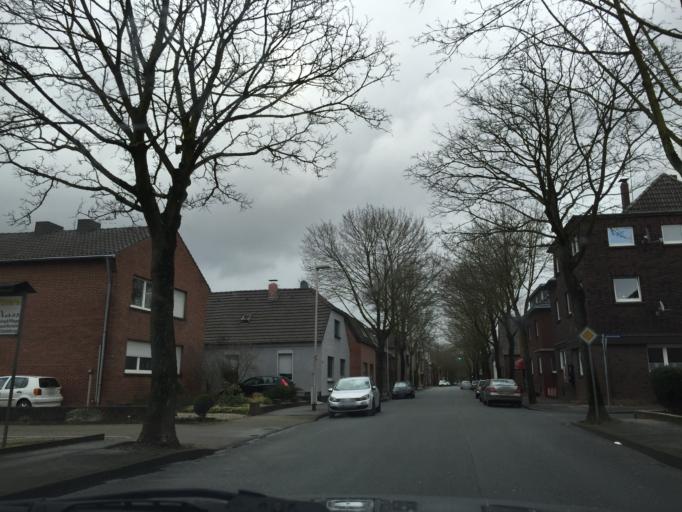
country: DE
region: North Rhine-Westphalia
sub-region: Regierungsbezirk Dusseldorf
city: Kleve
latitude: 51.7924
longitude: 6.1573
